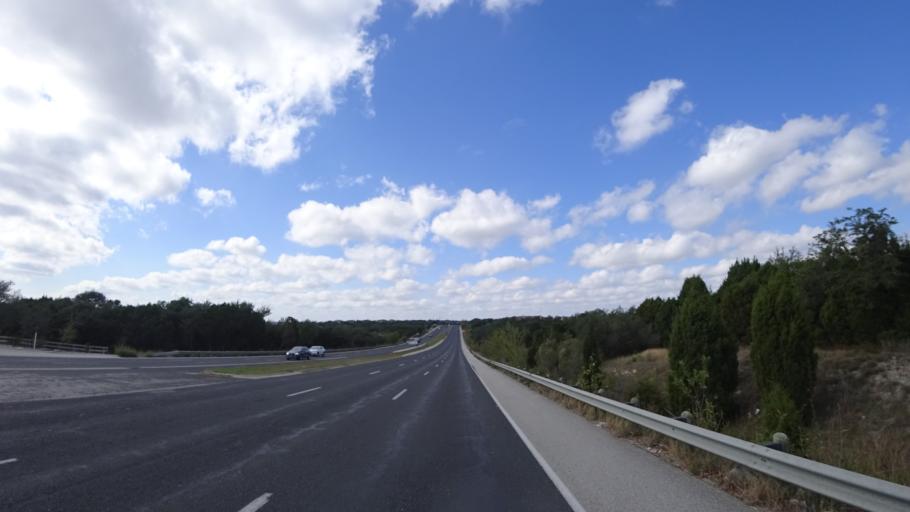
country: US
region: Texas
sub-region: Travis County
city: Barton Creek
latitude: 30.2571
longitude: -97.8726
